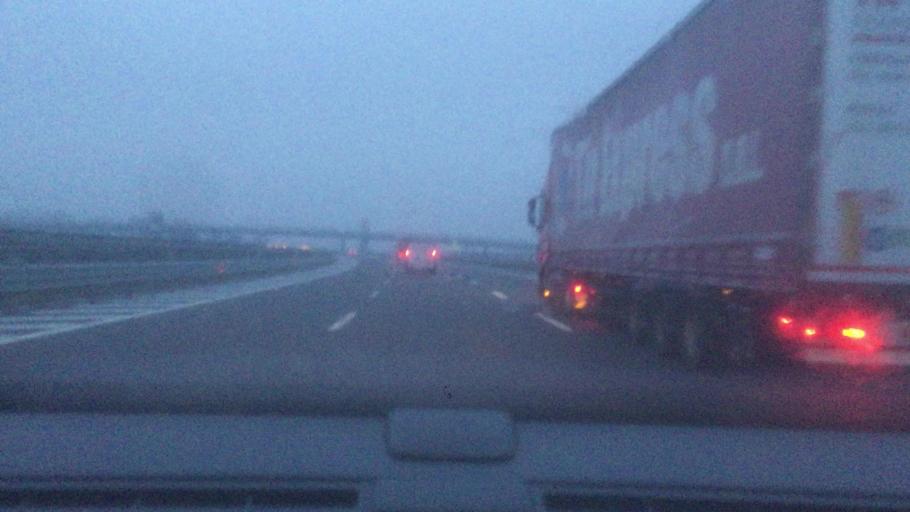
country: IT
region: Lombardy
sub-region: Provincia di Bergamo
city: Covo
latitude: 45.4879
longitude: 9.7648
